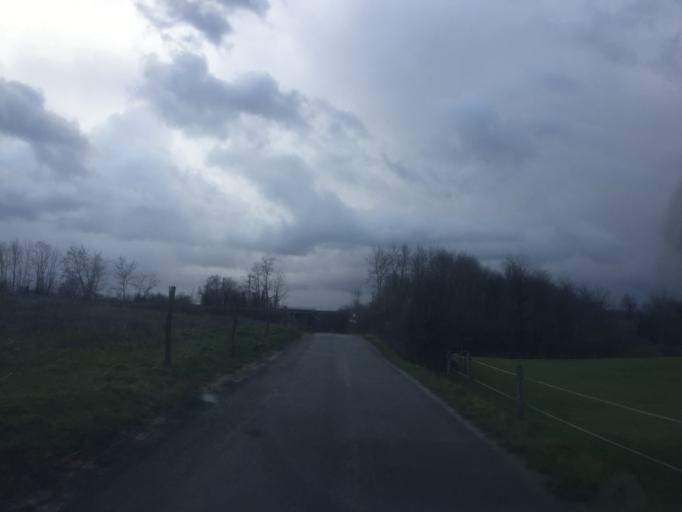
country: FR
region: Franche-Comte
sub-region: Departement du Jura
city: Fraisans
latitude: 47.1709
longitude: 5.7688
